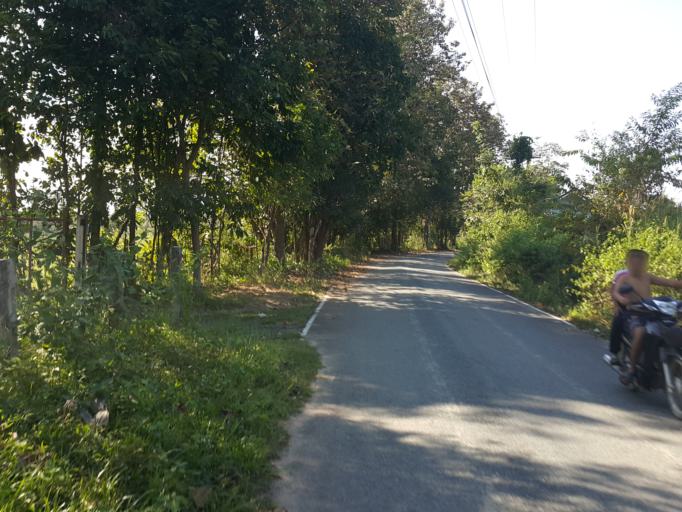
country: TH
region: Chiang Mai
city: Mae On
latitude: 18.7911
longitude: 99.1878
